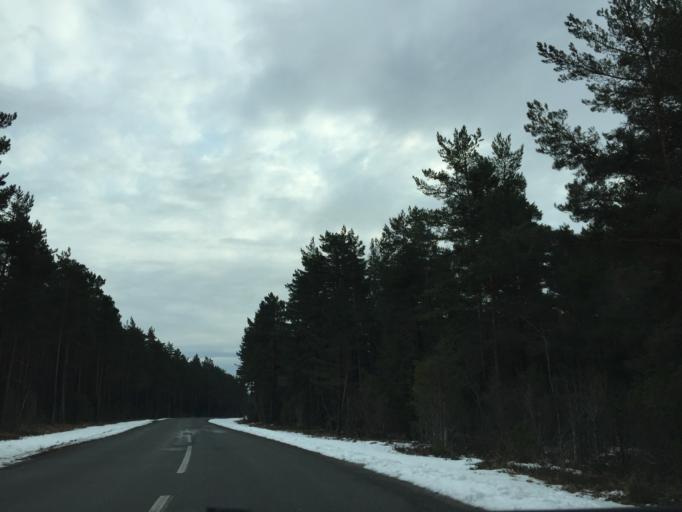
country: EE
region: Saare
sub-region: Kuressaare linn
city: Kuressaare
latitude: 58.4599
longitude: 22.0425
